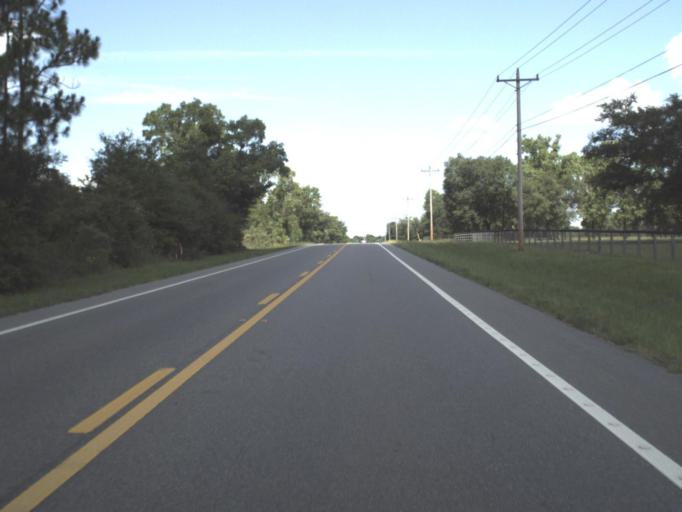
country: US
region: Florida
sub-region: Clay County
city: Keystone Heights
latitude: 29.7426
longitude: -81.9742
